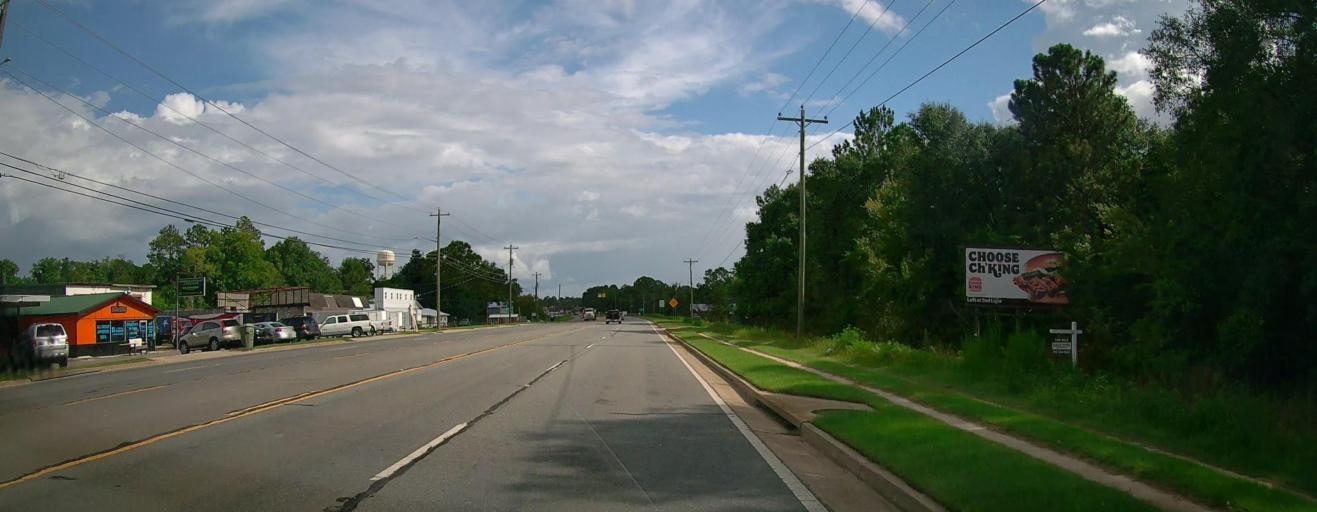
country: US
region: Georgia
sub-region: Coffee County
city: Douglas
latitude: 31.5311
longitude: -82.8511
